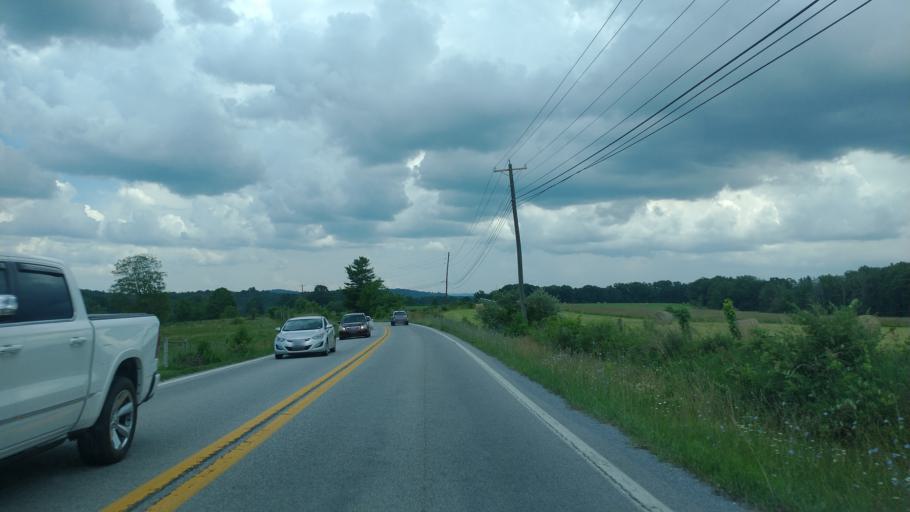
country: US
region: West Virginia
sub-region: Mercer County
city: Athens
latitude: 37.4510
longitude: -81.0071
